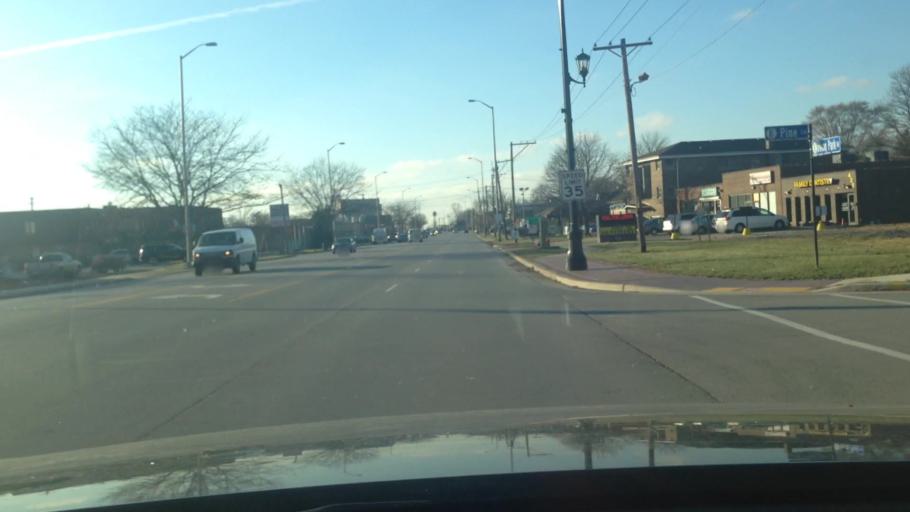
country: US
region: Illinois
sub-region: DuPage County
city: Wood Dale
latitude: 41.9612
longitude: -87.9635
